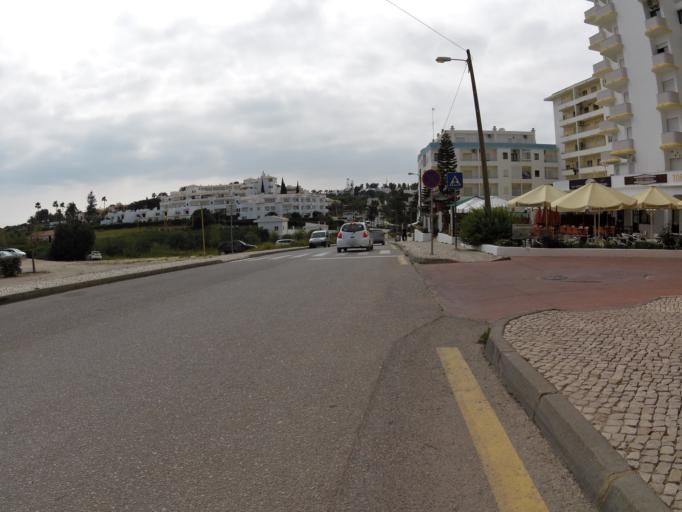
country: PT
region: Faro
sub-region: Silves
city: Armacao de Pera
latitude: 37.1032
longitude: -8.3688
